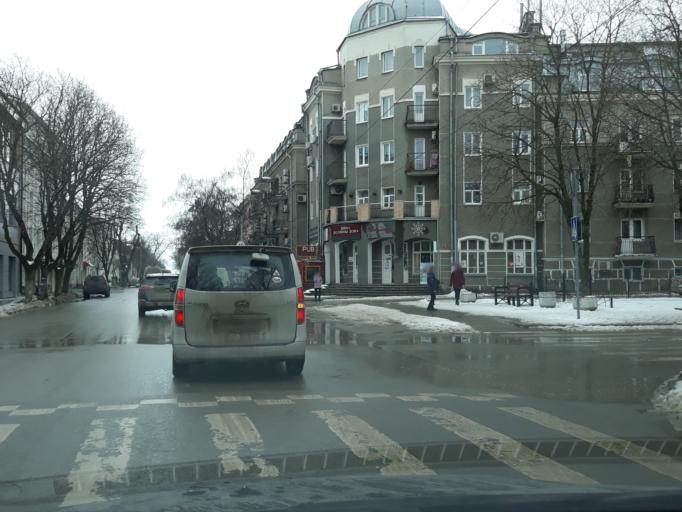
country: RU
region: Rostov
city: Taganrog
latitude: 47.2105
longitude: 38.9368
